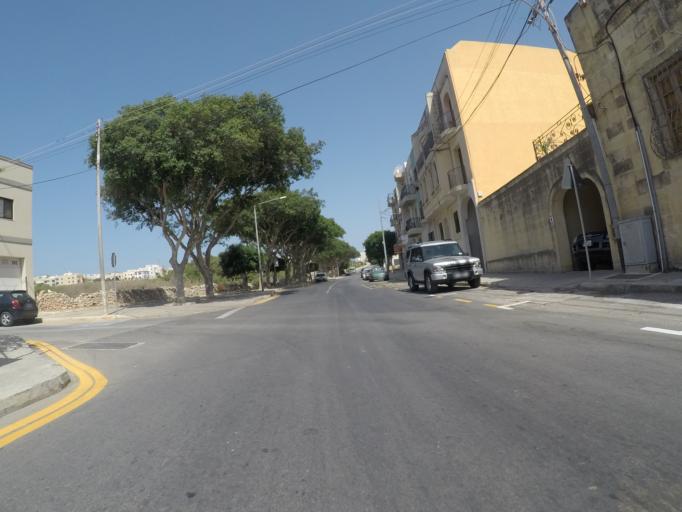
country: MT
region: L-Imgarr
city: Imgarr
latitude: 35.9195
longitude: 14.3695
